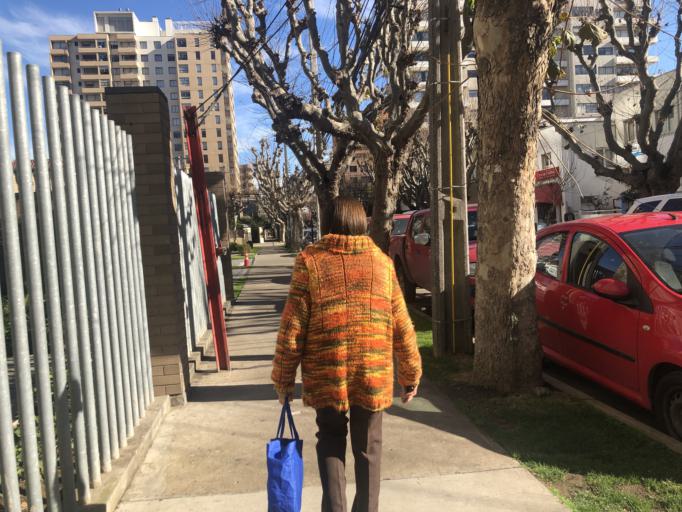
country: CL
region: Valparaiso
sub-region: Provincia de Valparaiso
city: Vina del Mar
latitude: -33.0213
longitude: -71.5531
